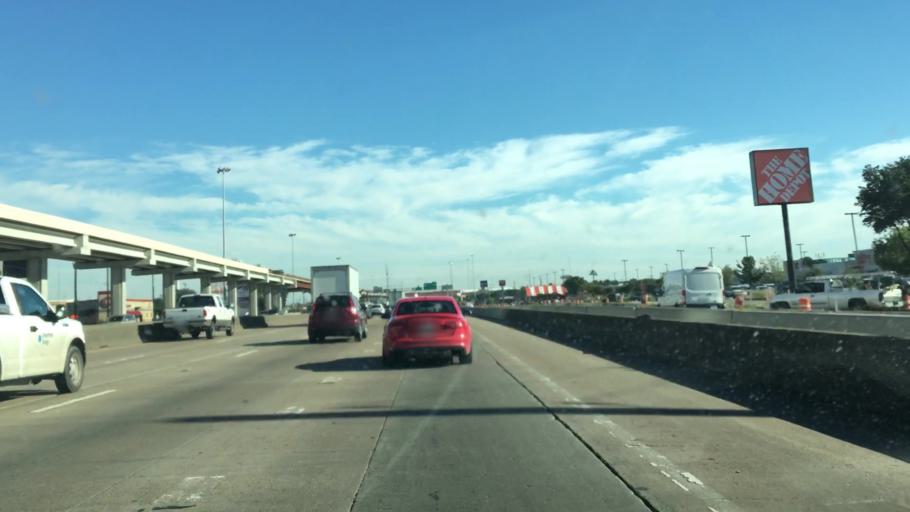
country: US
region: Texas
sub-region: Harris County
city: Galena Park
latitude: 29.7044
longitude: -95.3003
